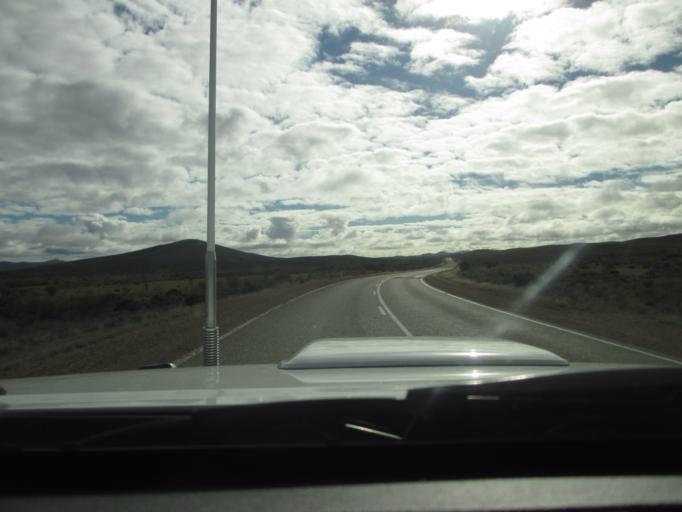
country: AU
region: South Australia
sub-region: Flinders Ranges
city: Quorn
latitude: -32.3038
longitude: 138.4855
